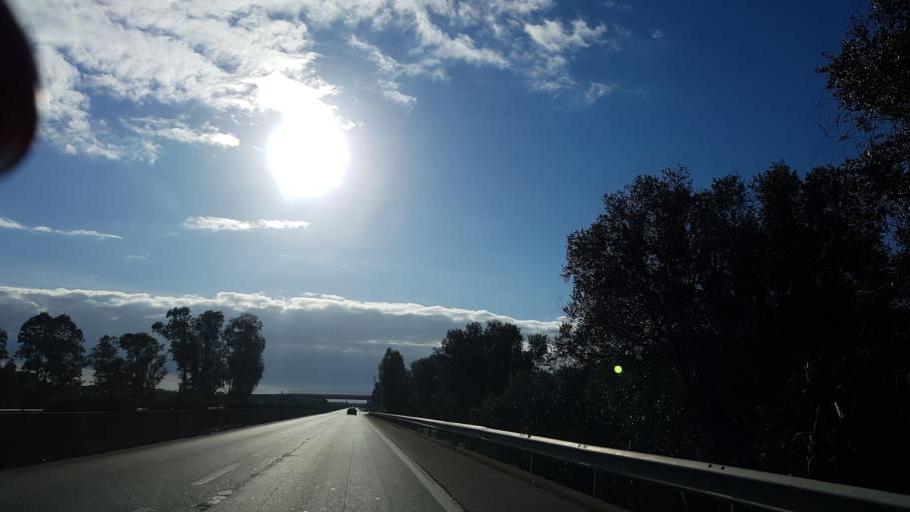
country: IT
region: Apulia
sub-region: Provincia di Brindisi
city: Tuturano
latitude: 40.5576
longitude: 17.9916
